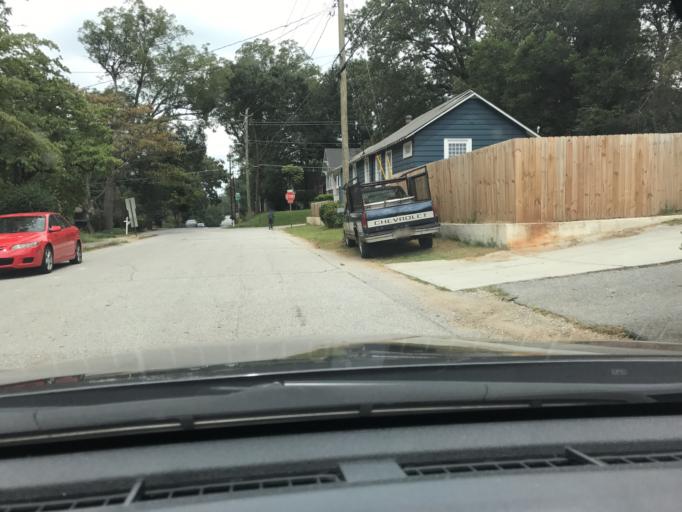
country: US
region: Georgia
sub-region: DeKalb County
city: Druid Hills
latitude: 33.7488
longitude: -84.3262
